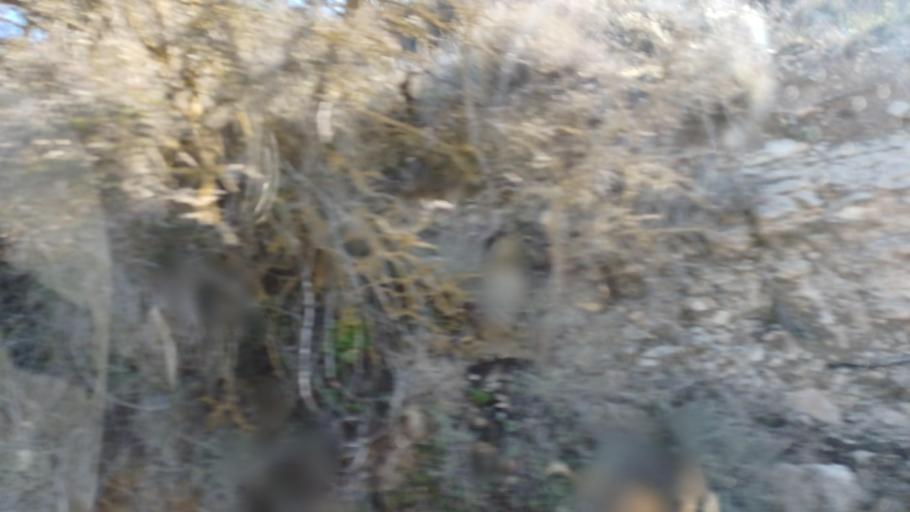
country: CY
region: Limassol
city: Pachna
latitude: 34.8133
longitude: 32.6640
